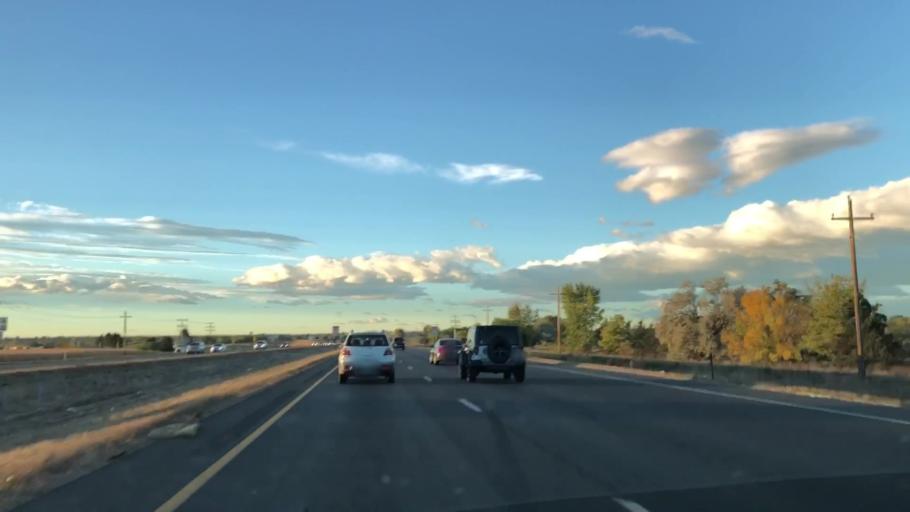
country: US
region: Colorado
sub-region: Weld County
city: Windsor
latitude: 40.5180
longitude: -104.9918
